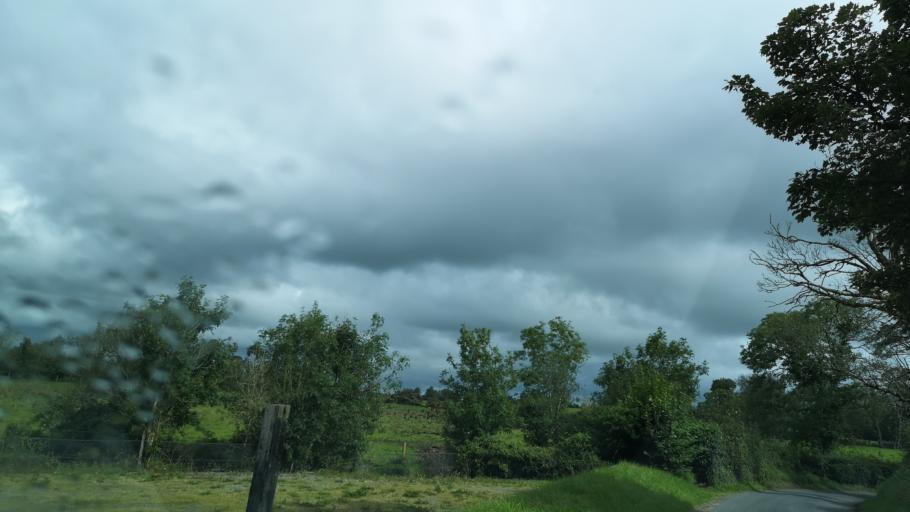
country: IE
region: Connaught
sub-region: County Galway
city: Loughrea
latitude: 53.3069
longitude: -8.5978
